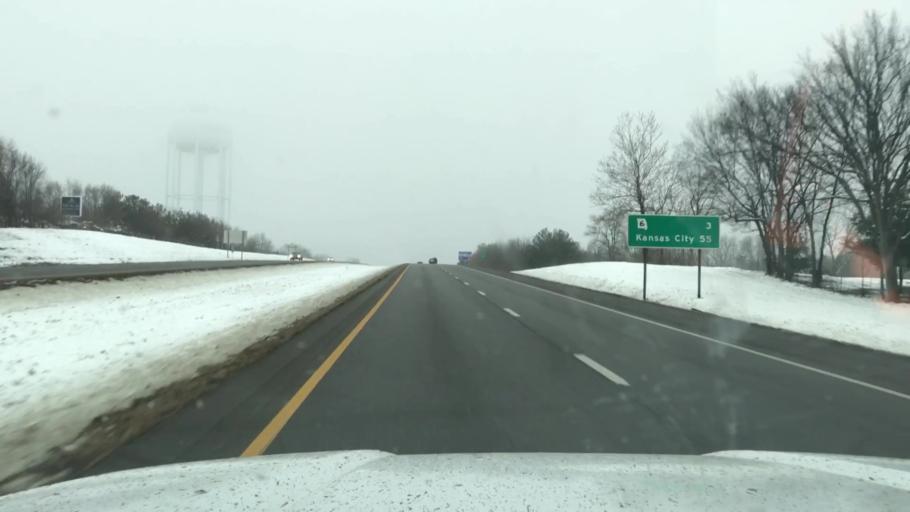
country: US
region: Missouri
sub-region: Andrew County
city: Country Club Village
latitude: 39.8013
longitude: -94.7994
